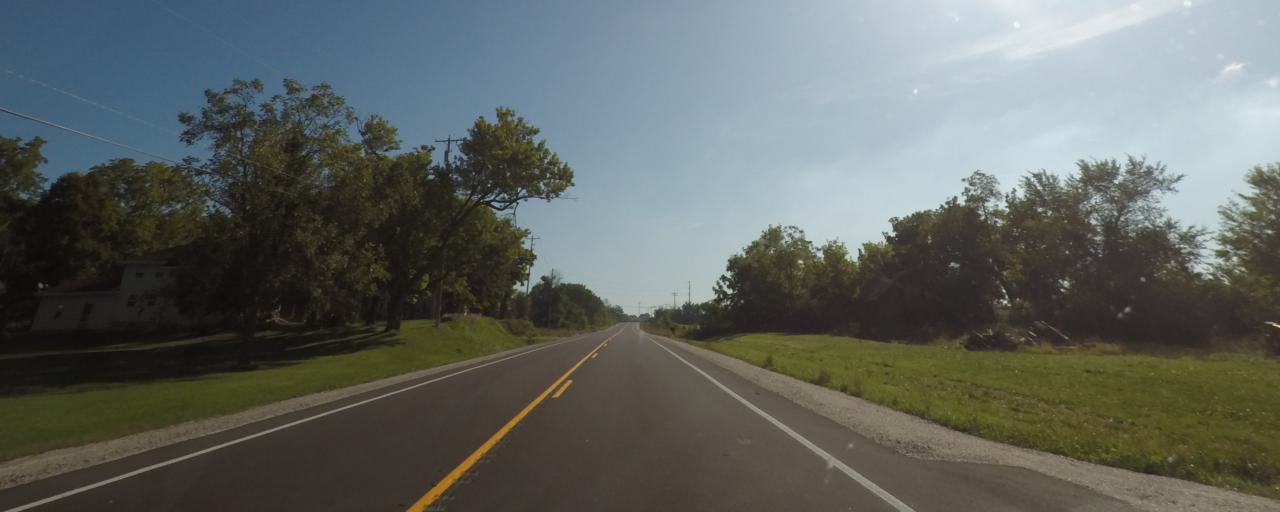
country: US
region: Wisconsin
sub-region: Jefferson County
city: Jefferson
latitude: 43.0168
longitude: -88.7405
